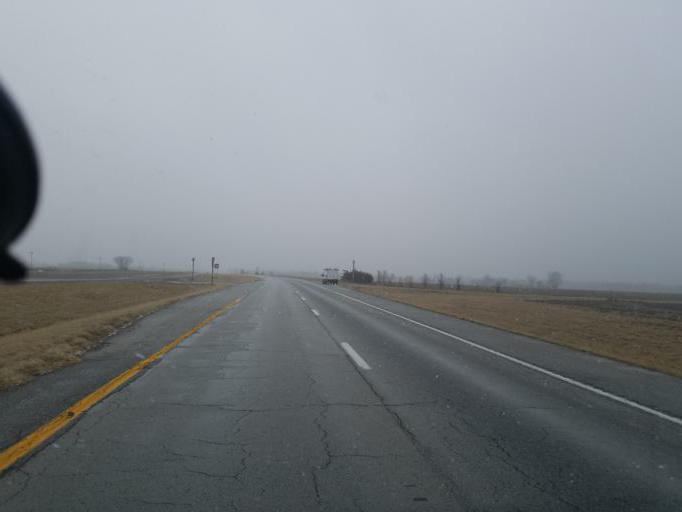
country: US
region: Missouri
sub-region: Macon County
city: La Plata
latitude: 39.9412
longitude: -92.4772
